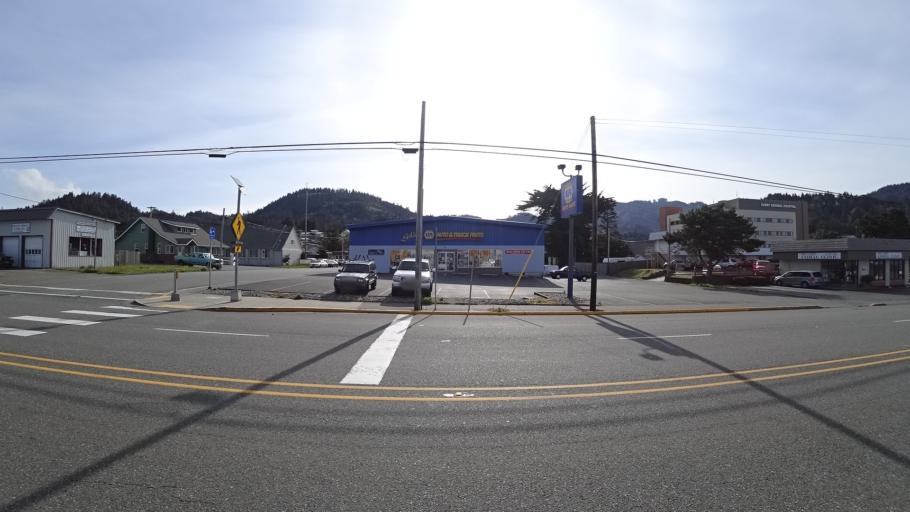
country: US
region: Oregon
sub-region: Curry County
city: Gold Beach
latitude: 42.4124
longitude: -124.4206
